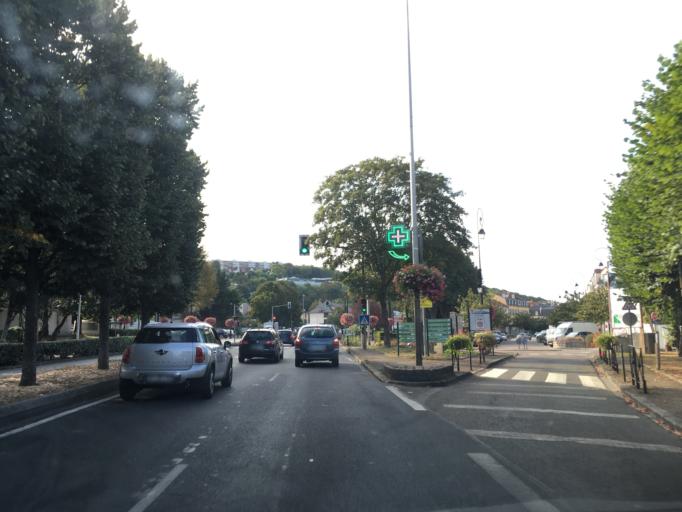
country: FR
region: Ile-de-France
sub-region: Departement des Yvelines
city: Le Port-Marly
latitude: 48.8785
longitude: 2.1132
